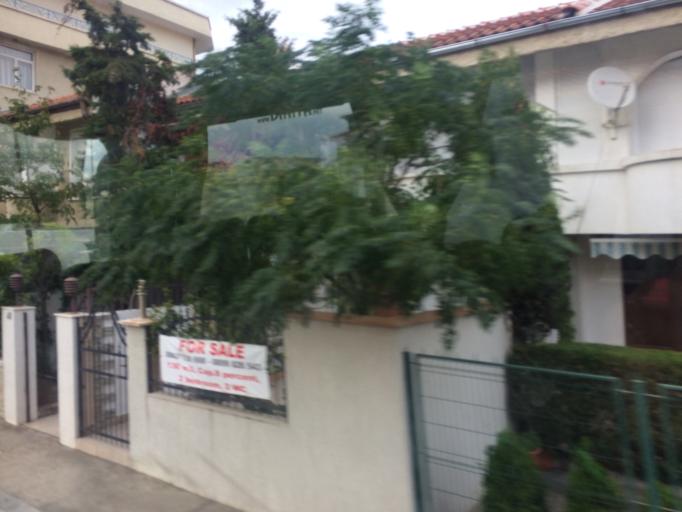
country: BG
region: Burgas
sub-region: Obshtina Nesebur
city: Sveti Vlas
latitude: 42.7122
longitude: 27.7556
